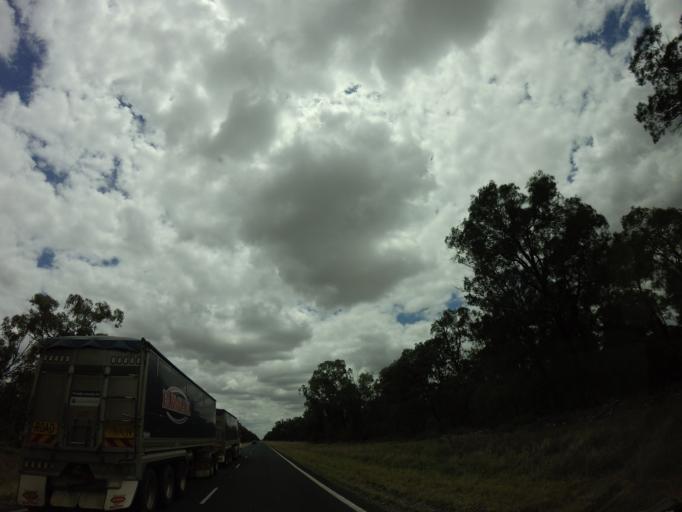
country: AU
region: Queensland
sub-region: Goondiwindi
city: Goondiwindi
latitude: -28.4230
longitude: 150.3033
